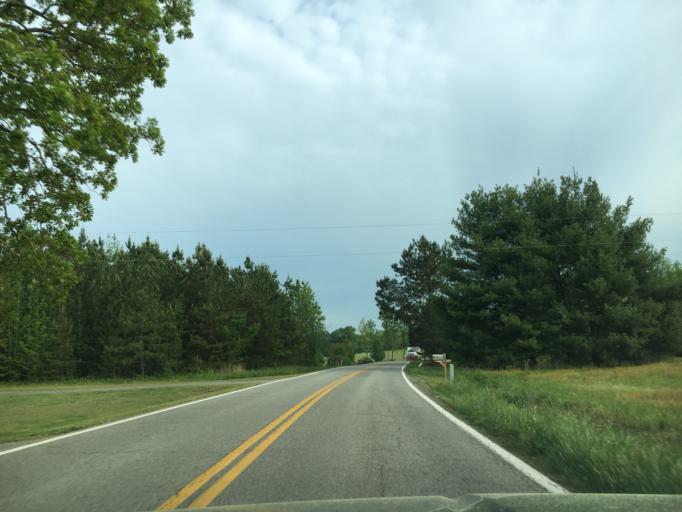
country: US
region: Virginia
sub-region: Halifax County
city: Halifax
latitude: 36.8854
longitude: -78.7956
